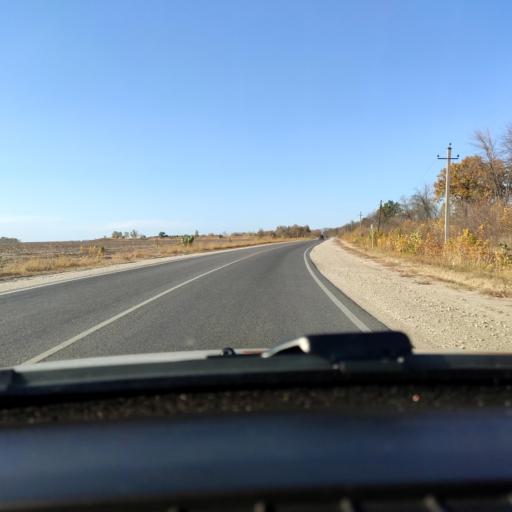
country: RU
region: Voronezj
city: Semiluki
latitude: 51.7236
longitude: 38.9931
